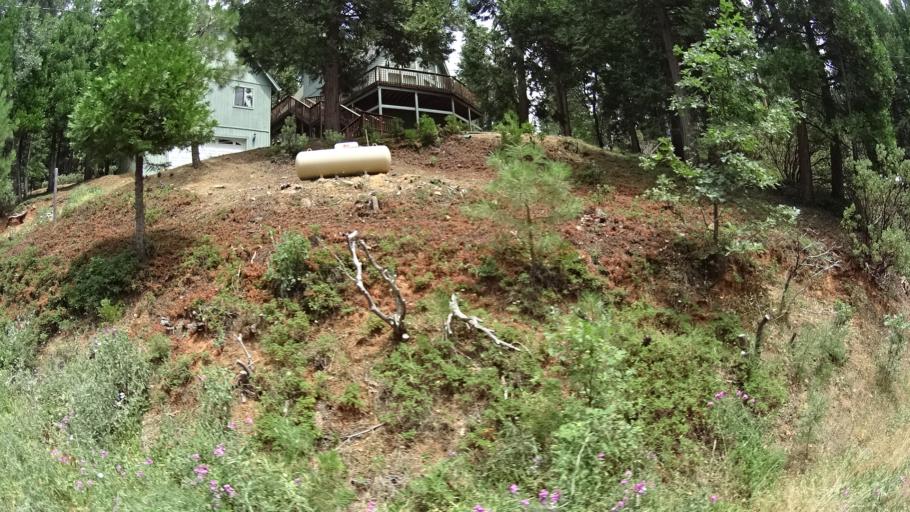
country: US
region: California
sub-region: Calaveras County
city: Arnold
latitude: 38.2344
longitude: -120.3561
